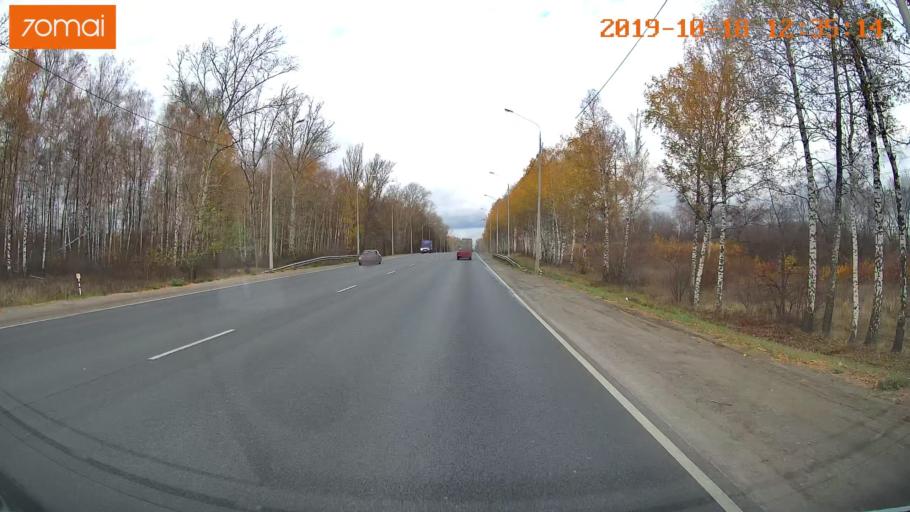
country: RU
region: Rjazan
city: Ryazan'
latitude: 54.6223
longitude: 39.6361
